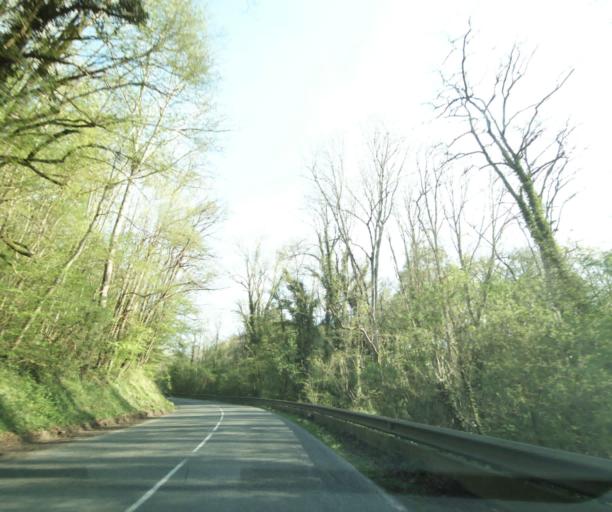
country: FR
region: Ile-de-France
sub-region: Departement de Seine-et-Marne
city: Vernou-la-Celle-sur-Seine
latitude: 48.3989
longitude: 2.8317
